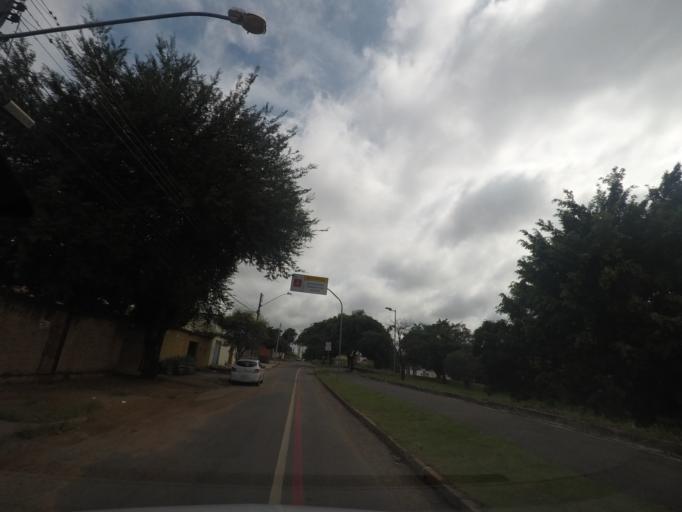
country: BR
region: Goias
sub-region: Goiania
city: Goiania
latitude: -16.7274
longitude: -49.2595
